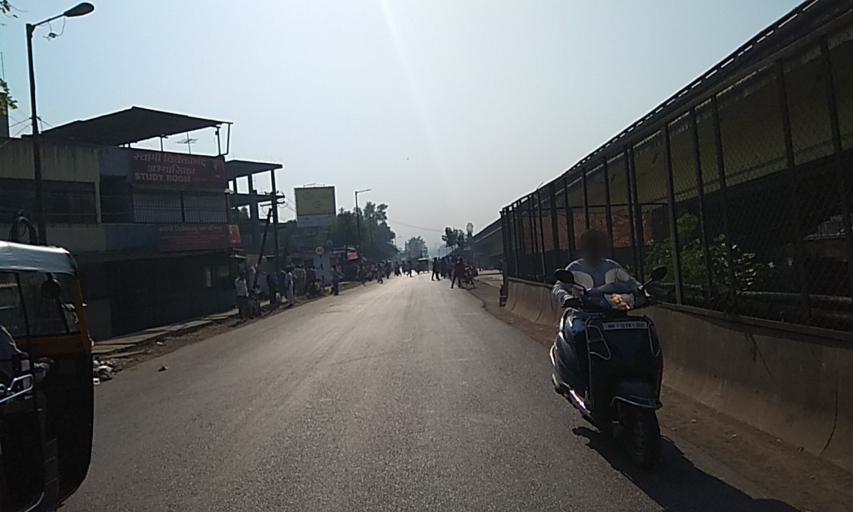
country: IN
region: Maharashtra
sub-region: Pune Division
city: Kharakvasla
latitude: 18.4793
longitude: 73.8054
